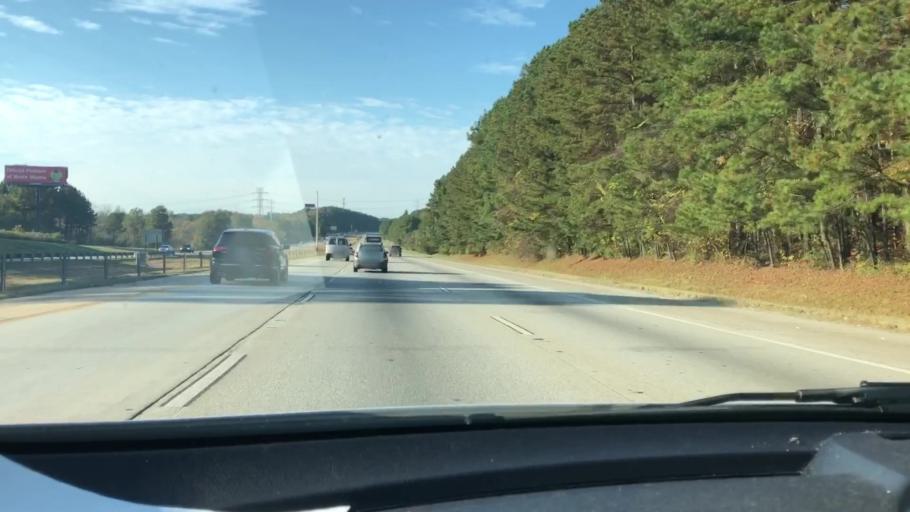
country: US
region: Georgia
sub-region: Clayton County
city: Conley
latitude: 33.6448
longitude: -84.3153
